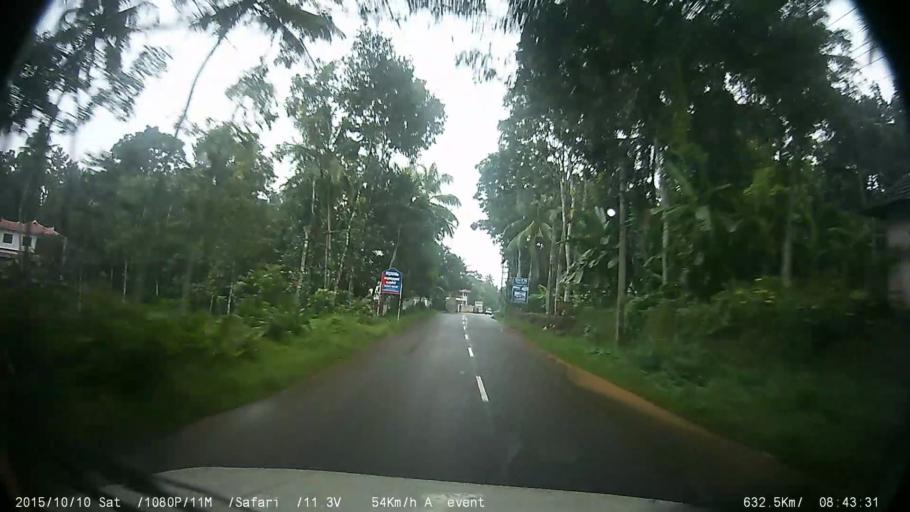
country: IN
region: Kerala
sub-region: Kottayam
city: Palackattumala
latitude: 9.7474
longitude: 76.5341
